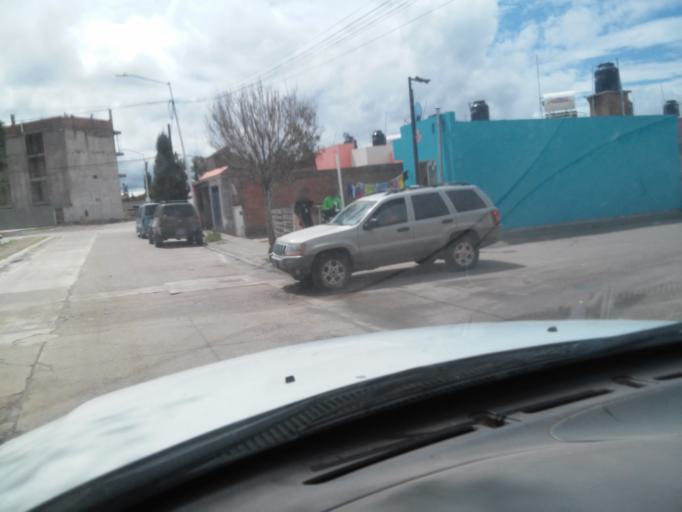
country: MX
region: Durango
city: Victoria de Durango
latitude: 24.0201
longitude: -104.6120
